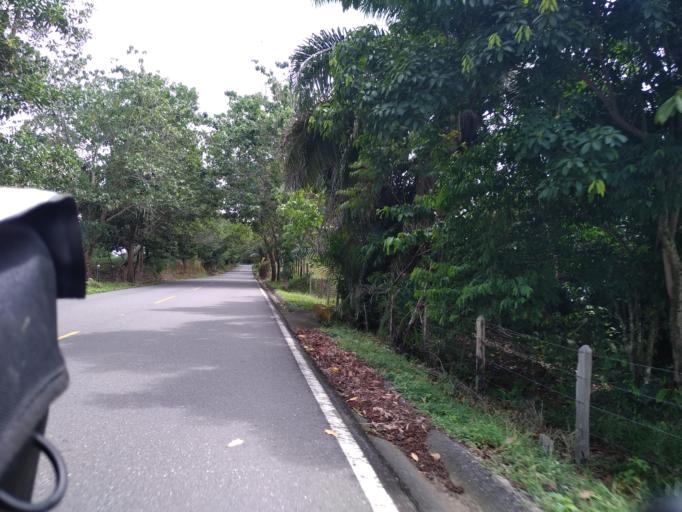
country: CO
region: Santander
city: Cimitarra
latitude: 6.4653
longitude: -74.0290
